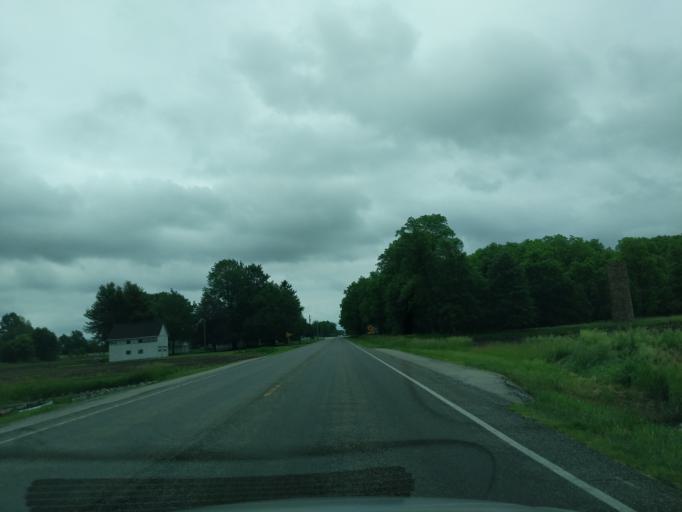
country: US
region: Indiana
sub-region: Tipton County
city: Tipton
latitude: 40.2833
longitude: -85.9696
